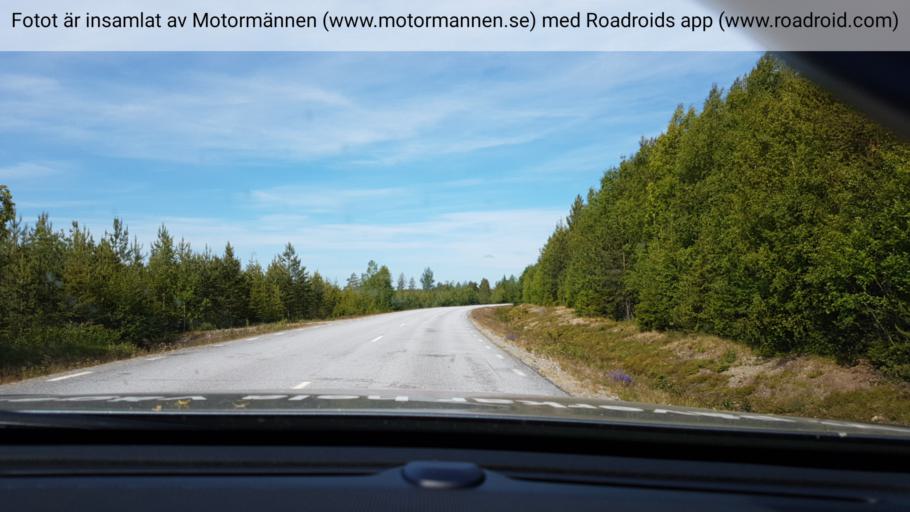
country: SE
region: Vaesterbotten
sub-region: Asele Kommun
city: Asele
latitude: 64.1833
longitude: 17.2128
